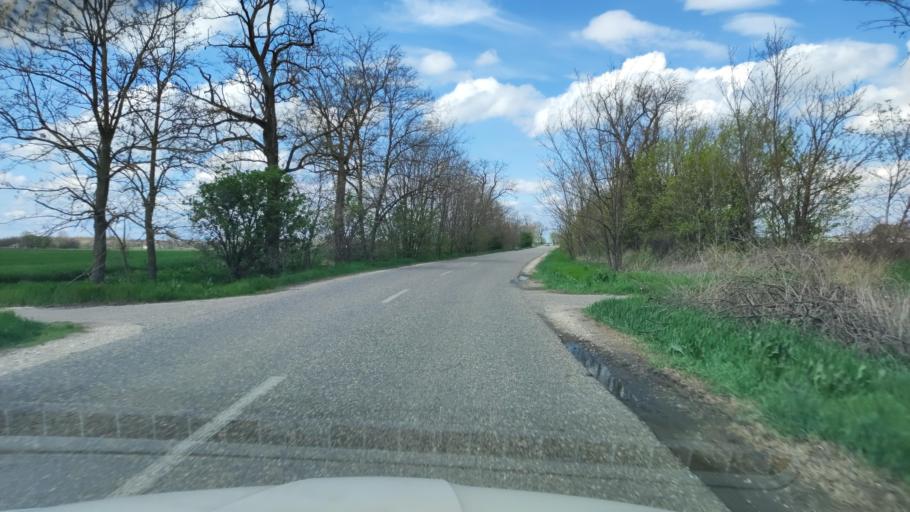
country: HU
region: Pest
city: Tortel
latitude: 47.1298
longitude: 19.9177
